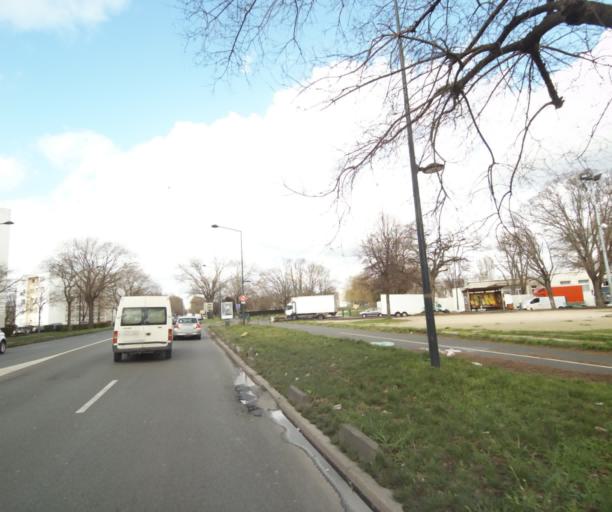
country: FR
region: Ile-de-France
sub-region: Departement de Seine-Saint-Denis
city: Saint-Denis
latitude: 48.9380
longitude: 2.3711
